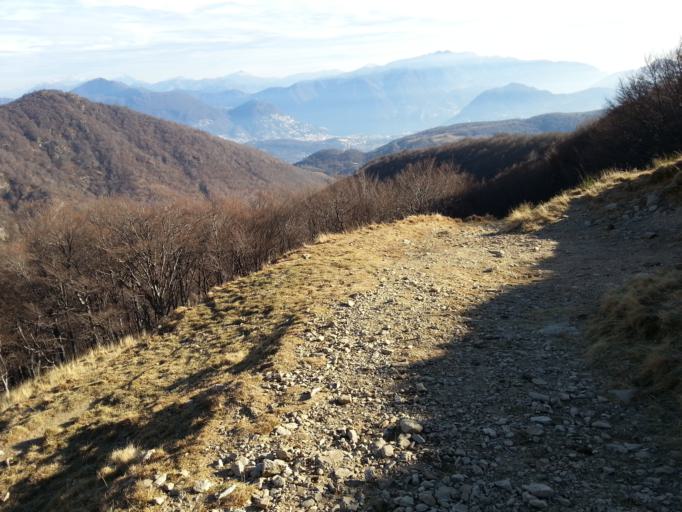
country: CH
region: Ticino
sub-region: Lugano District
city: Gravesano
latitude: 46.0632
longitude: 8.8674
